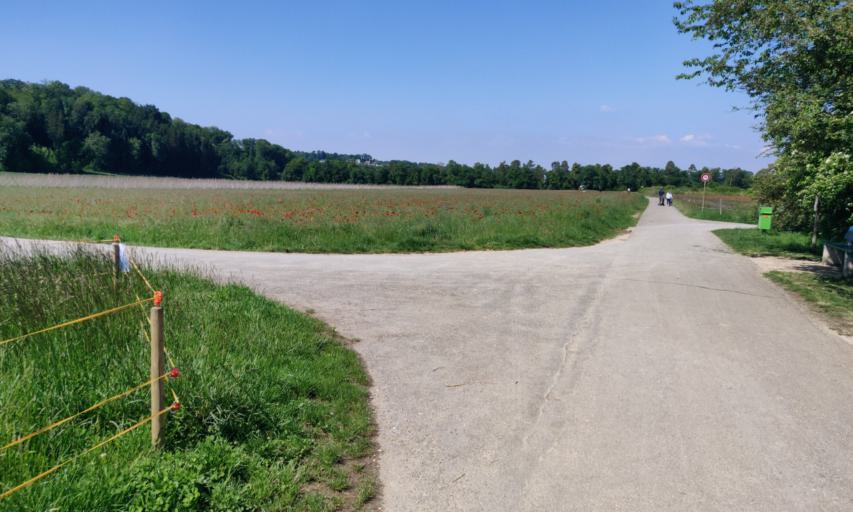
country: CH
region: Basel-Landschaft
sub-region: Bezirk Arlesheim
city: Aesch
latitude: 47.4791
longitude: 7.5848
